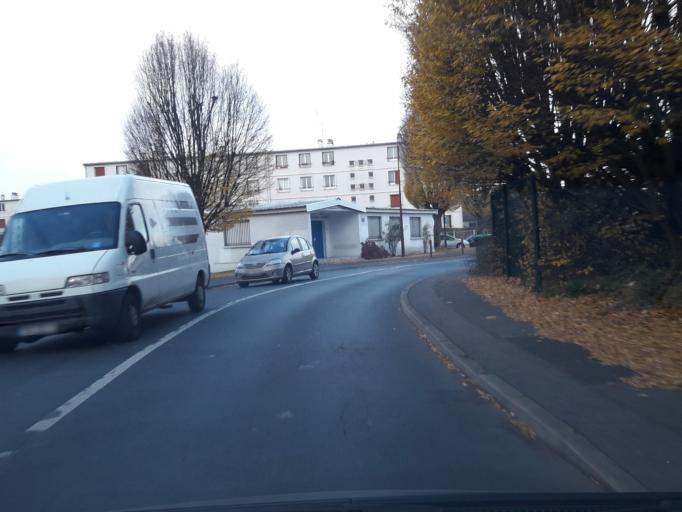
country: FR
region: Ile-de-France
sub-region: Departement de l'Essonne
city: Fleury-Merogis
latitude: 48.6443
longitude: 2.3467
